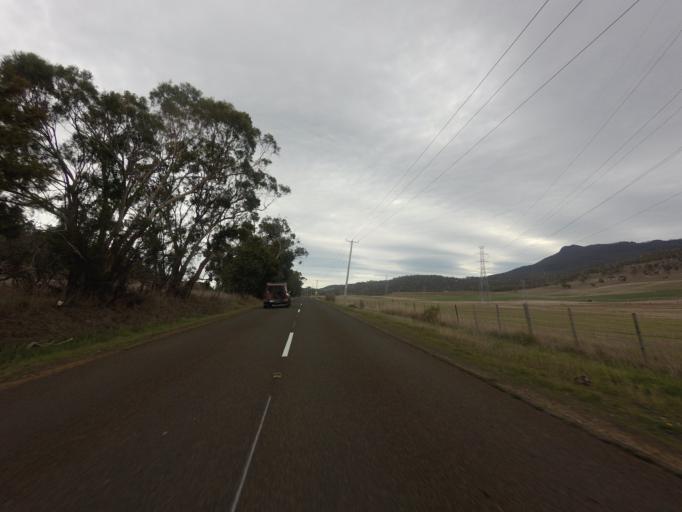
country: AU
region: Tasmania
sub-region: Brighton
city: Bridgewater
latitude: -42.6632
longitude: 147.1300
